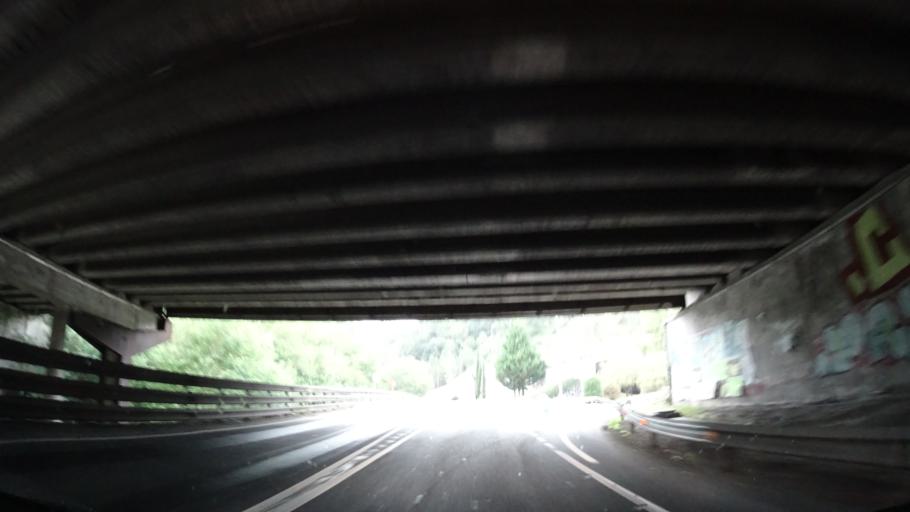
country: ES
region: Basque Country
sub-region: Bizkaia
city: Galdakao
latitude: 43.2298
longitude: -2.8194
